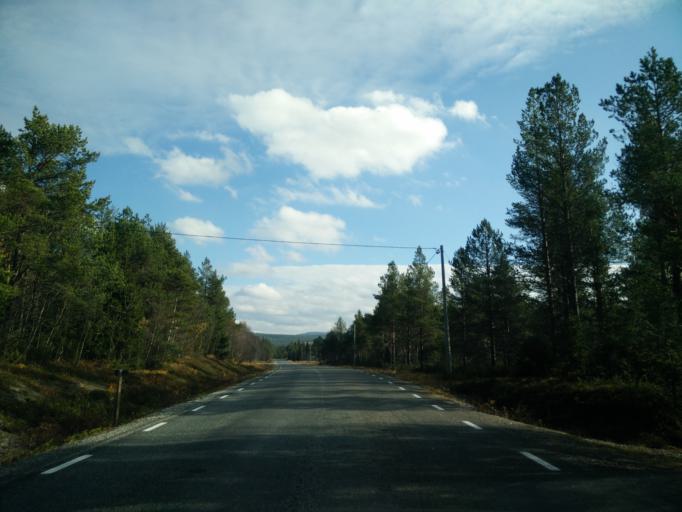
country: SE
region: Jaemtland
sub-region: Are Kommun
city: Are
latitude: 62.5500
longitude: 12.5820
